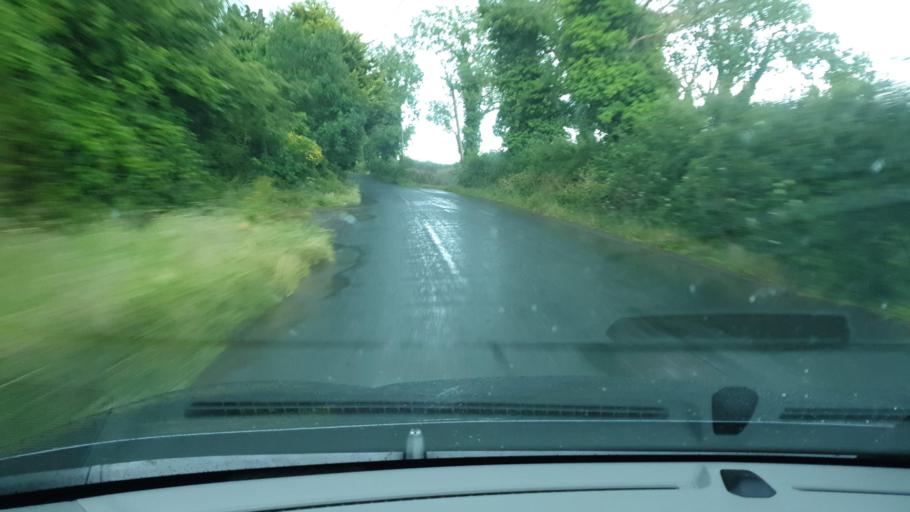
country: IE
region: Leinster
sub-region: An Mhi
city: Navan
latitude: 53.6294
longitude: -6.6743
